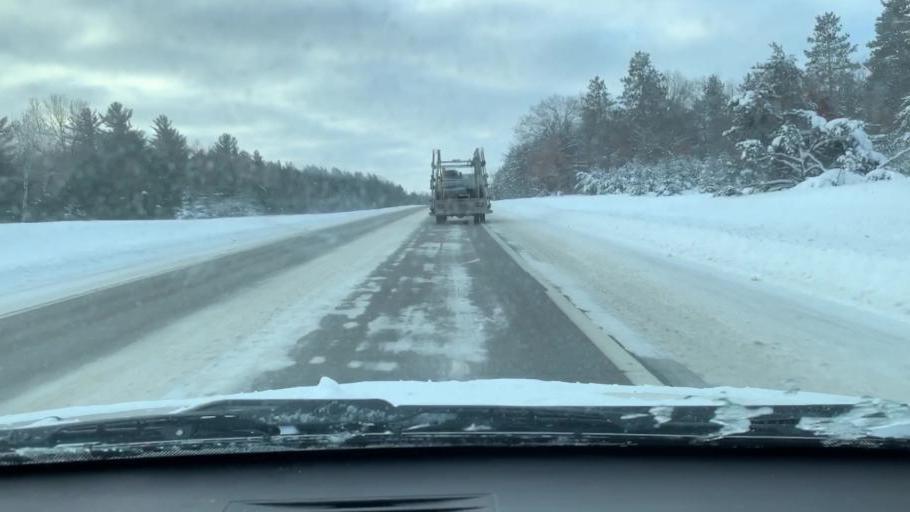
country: US
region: Michigan
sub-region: Wexford County
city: Manton
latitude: 44.4807
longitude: -85.4065
